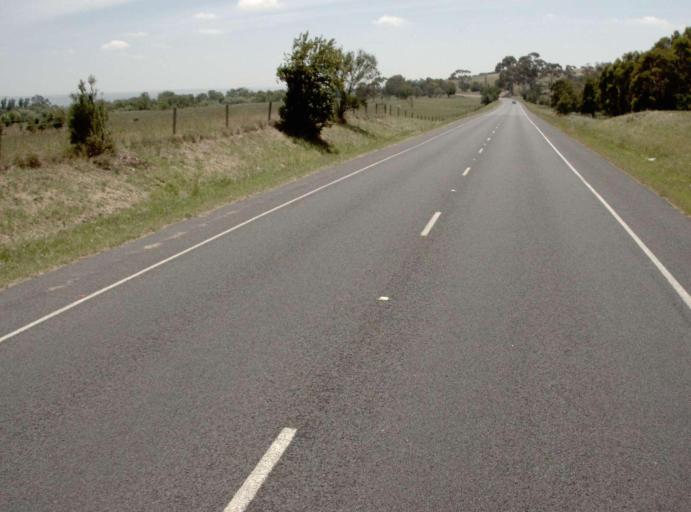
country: AU
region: Victoria
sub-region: Latrobe
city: Traralgon
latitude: -38.2243
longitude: 146.5438
